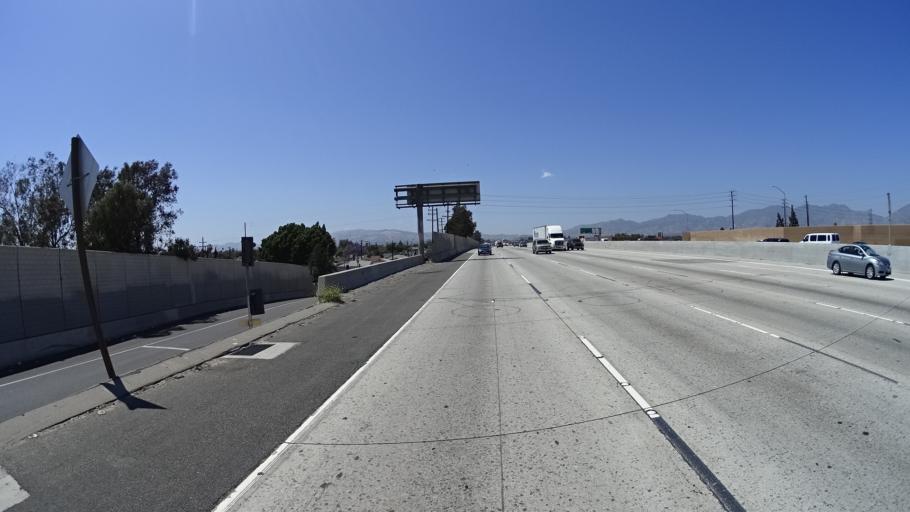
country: US
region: California
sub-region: Los Angeles County
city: San Fernando
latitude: 34.2500
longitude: -118.4284
